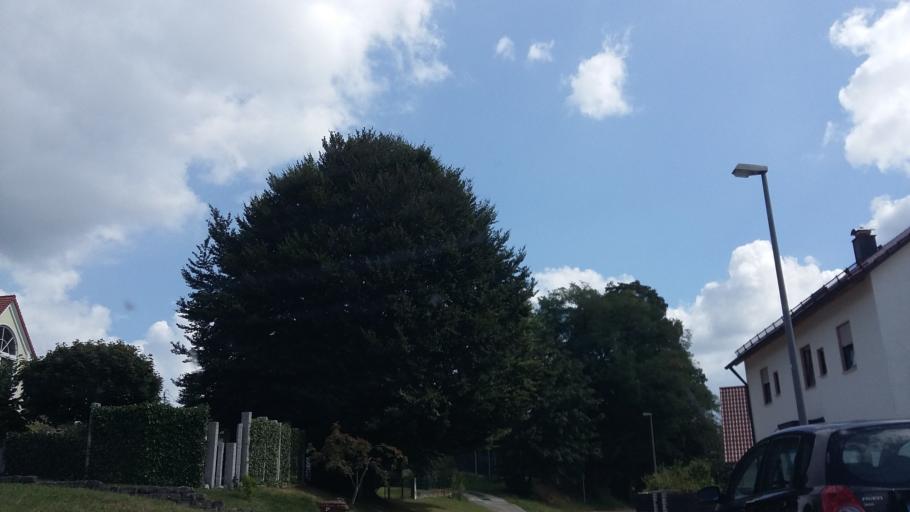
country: DE
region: Bavaria
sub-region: Swabia
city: Jettingen-Scheppach
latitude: 48.4034
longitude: 10.4559
